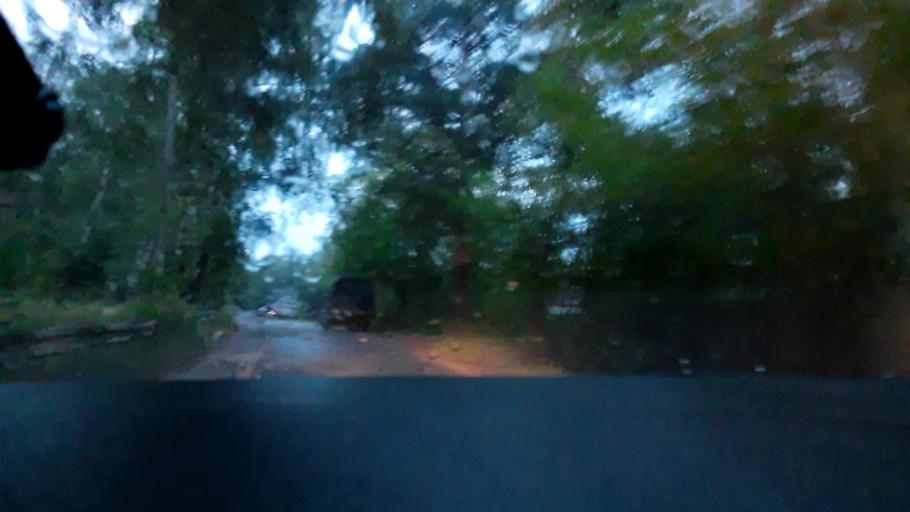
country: RU
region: Moscow
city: Rublevo
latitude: 55.7987
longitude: 37.3535
